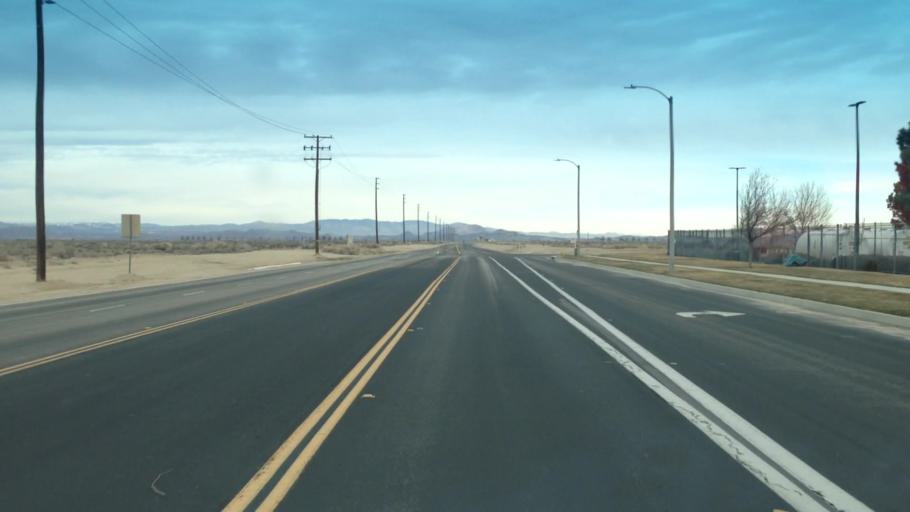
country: US
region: California
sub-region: Los Angeles County
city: Lancaster
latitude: 34.7247
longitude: -118.1838
